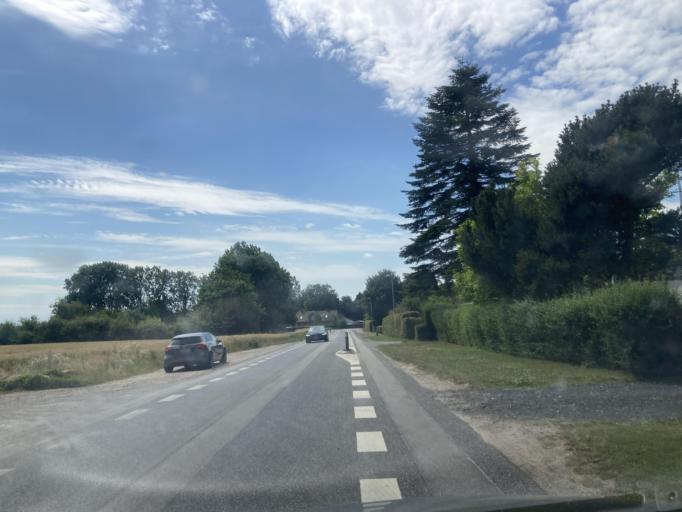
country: DK
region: Zealand
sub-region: Solrod Kommune
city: Solrod
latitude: 55.5277
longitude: 12.1675
